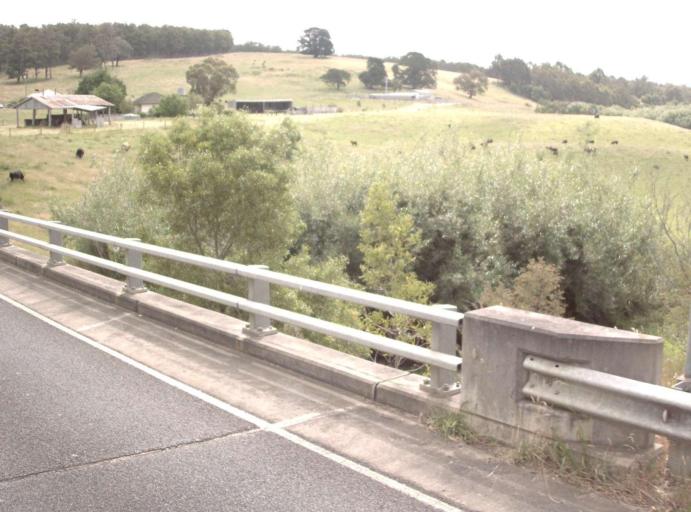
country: AU
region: Victoria
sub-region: Latrobe
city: Traralgon
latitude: -38.4089
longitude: 146.8224
